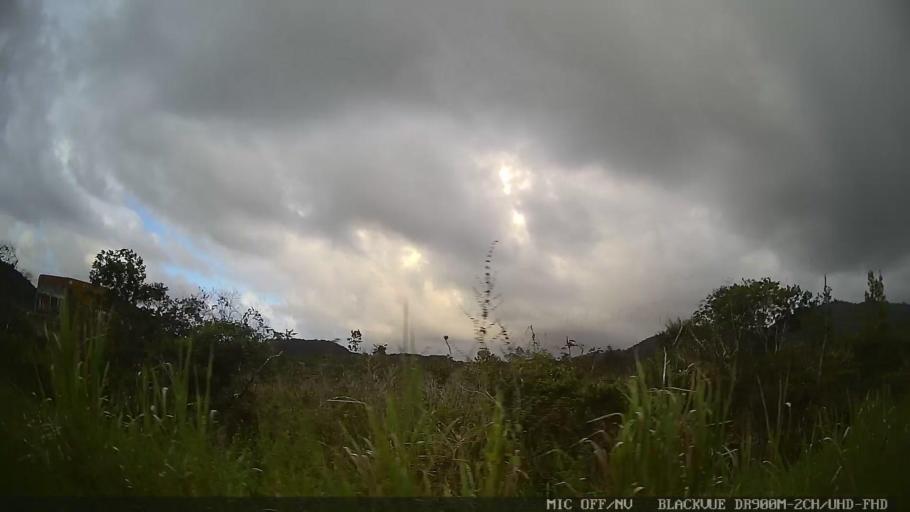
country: BR
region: Sao Paulo
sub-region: Itanhaem
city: Itanhaem
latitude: -24.1312
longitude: -46.7798
